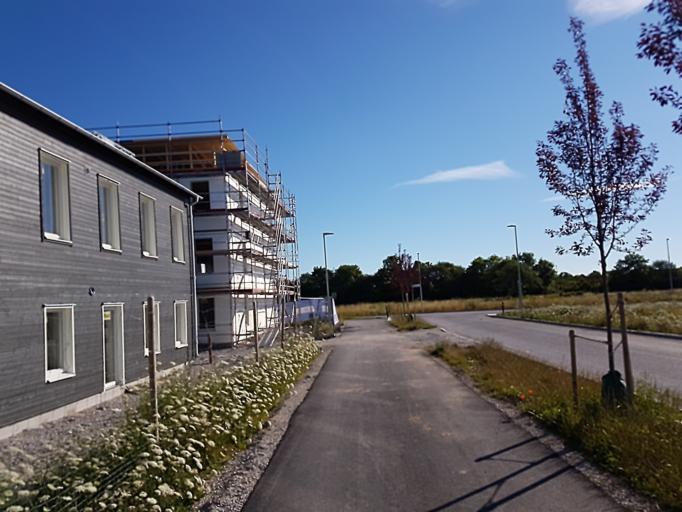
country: SE
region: Gotland
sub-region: Gotland
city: Visby
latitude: 57.6264
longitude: 18.3109
